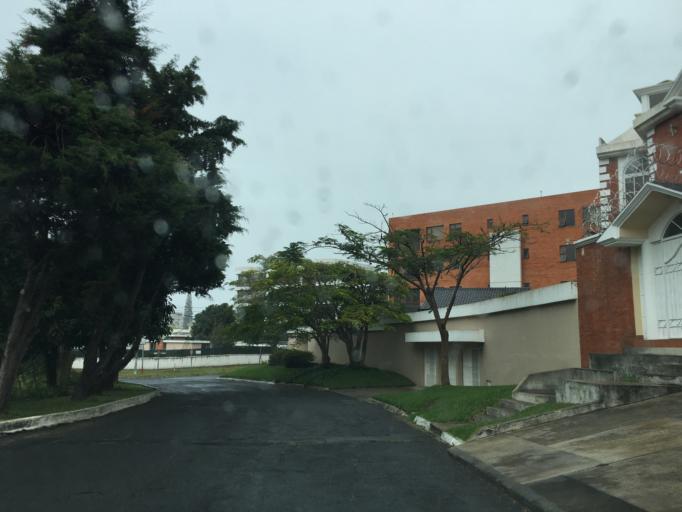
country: GT
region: Guatemala
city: Santa Catarina Pinula
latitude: 14.5857
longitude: -90.4930
